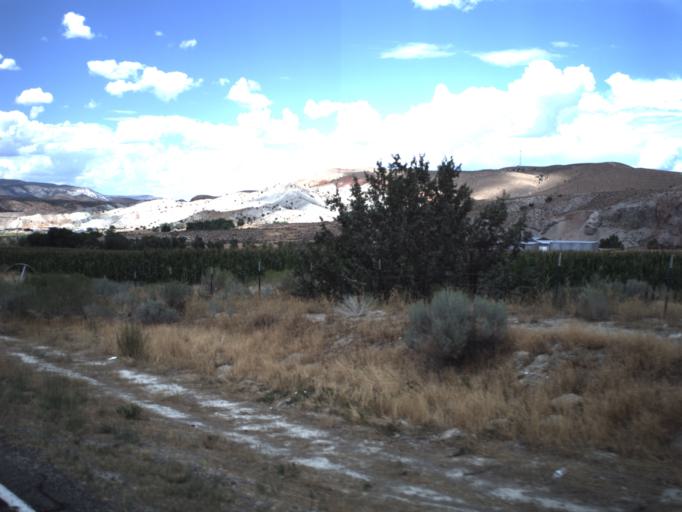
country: US
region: Utah
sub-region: Sanpete County
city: Centerfield
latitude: 39.1325
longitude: -111.7281
